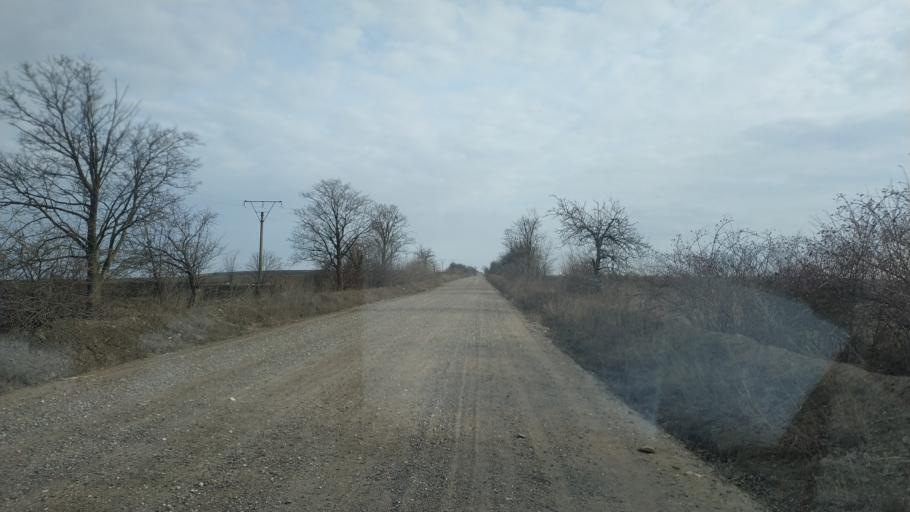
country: MD
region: Chisinau
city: Vadul lui Voda
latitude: 46.9818
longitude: 29.0835
